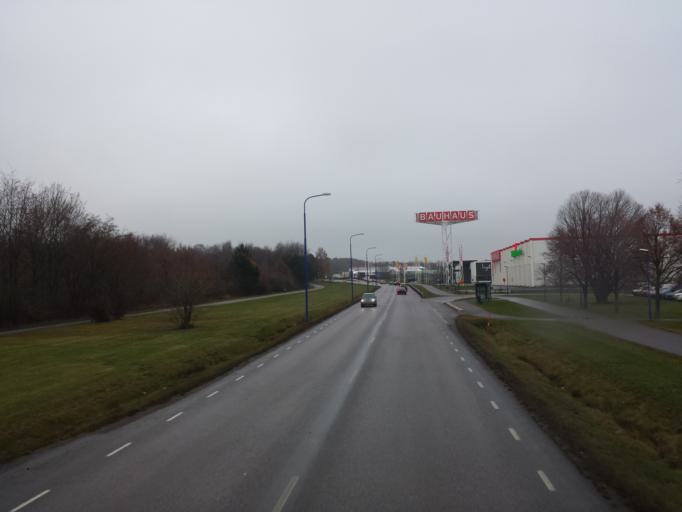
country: SE
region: OEstergoetland
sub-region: Norrkopings Kommun
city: Norrkoping
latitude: 58.6082
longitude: 16.1675
